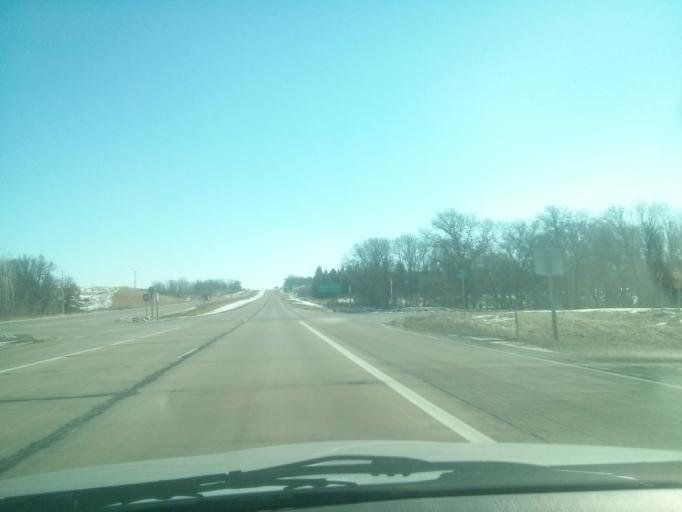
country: US
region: Wisconsin
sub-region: Saint Croix County
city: Somerset
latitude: 45.1226
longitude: -92.6117
